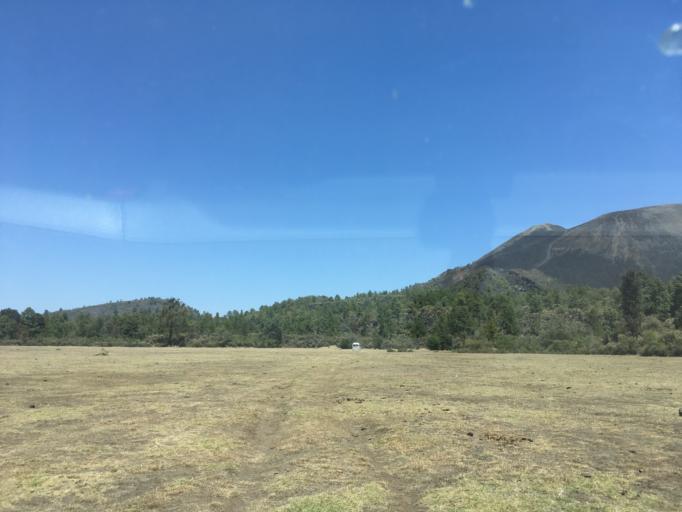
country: MX
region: Michoacan
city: Angahuan
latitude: 19.4827
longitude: -102.2532
